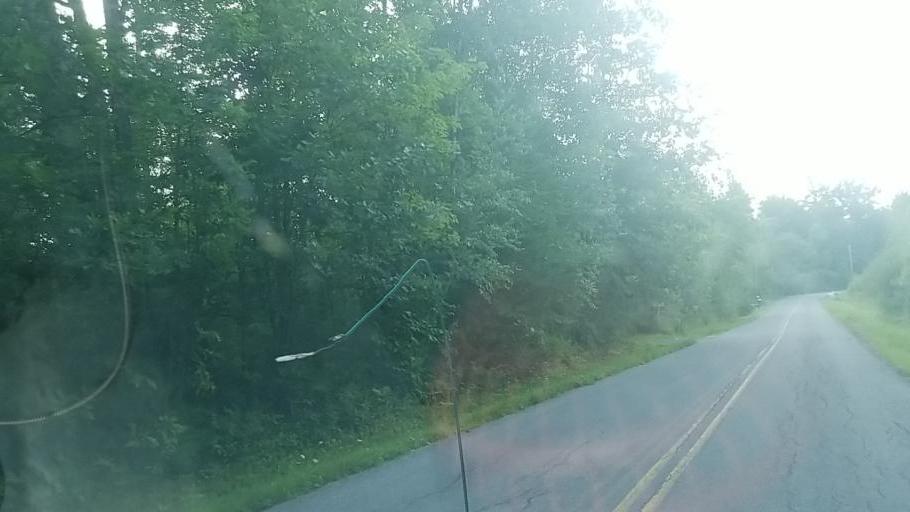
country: US
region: New York
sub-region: Fulton County
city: Broadalbin
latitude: 43.0792
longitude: -74.2244
